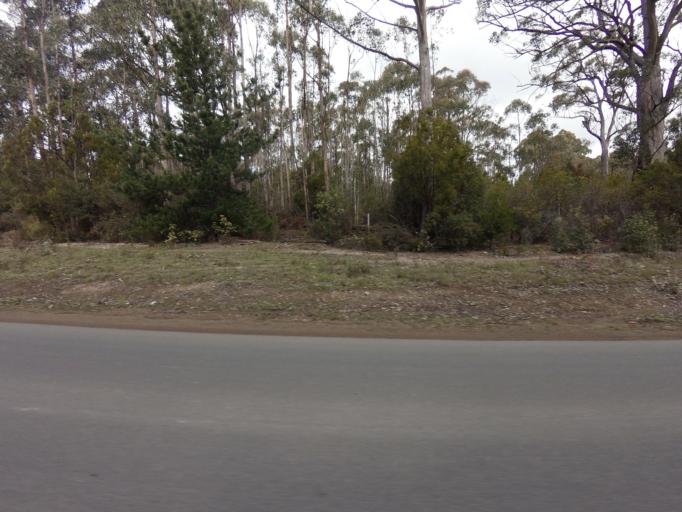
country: AU
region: Tasmania
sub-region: Huon Valley
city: Geeveston
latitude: -43.3233
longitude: 146.9835
